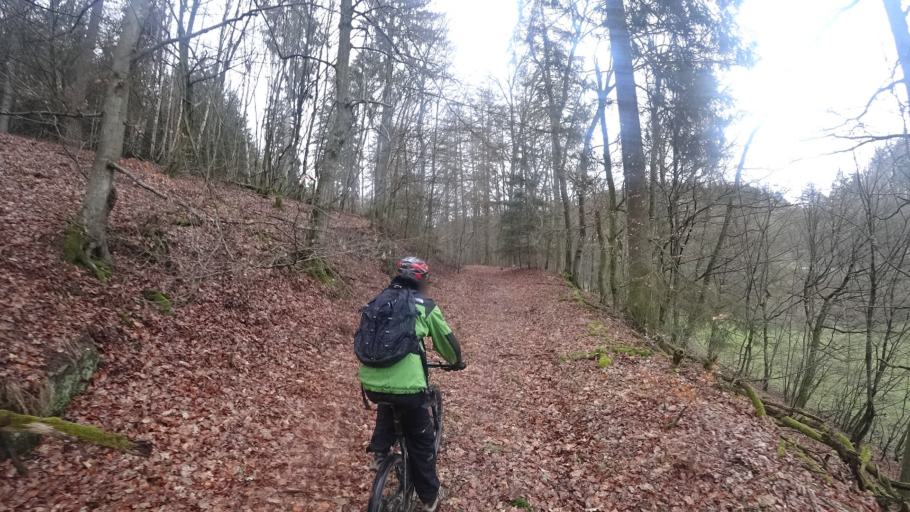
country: DE
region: Rheinland-Pfalz
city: Weidenbach
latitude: 50.1508
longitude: 7.8746
